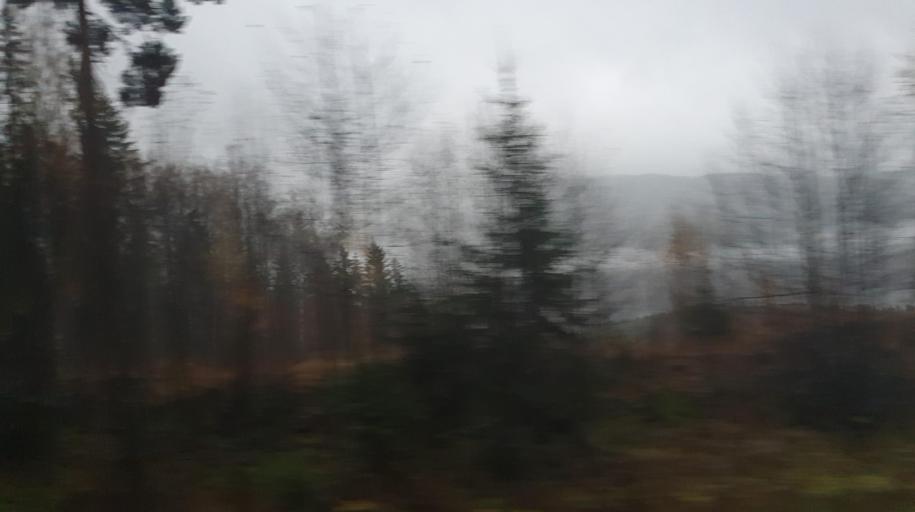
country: NO
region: Buskerud
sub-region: Krodsherad
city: Noresund
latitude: 60.1954
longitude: 9.5908
